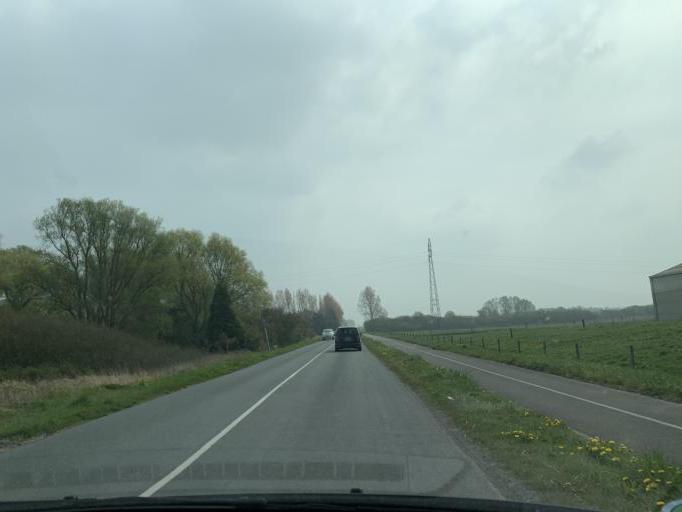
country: FR
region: Nord-Pas-de-Calais
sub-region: Departement du Nord
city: Leffrinckoucke
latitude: 51.0439
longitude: 2.4478
